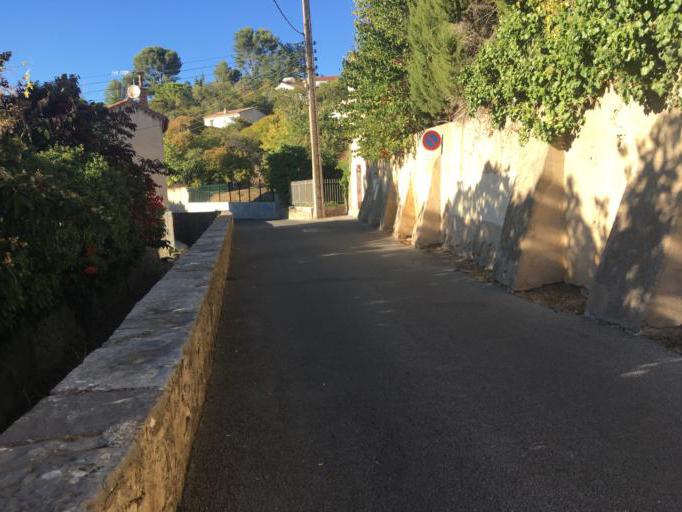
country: FR
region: Provence-Alpes-Cote d'Azur
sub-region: Departement du Var
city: Draguignan
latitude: 43.5425
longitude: 6.4635
